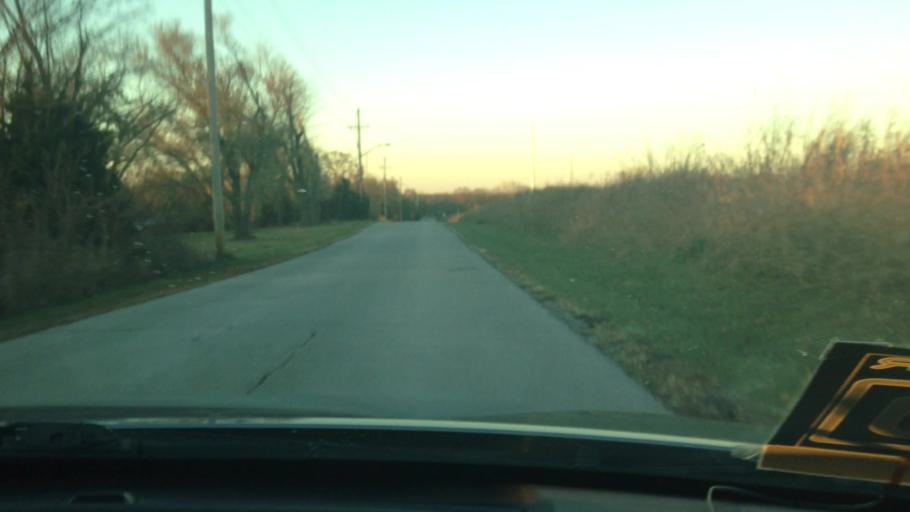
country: US
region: Kansas
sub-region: Wyandotte County
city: Bonner Springs
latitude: 39.1230
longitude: -94.8538
